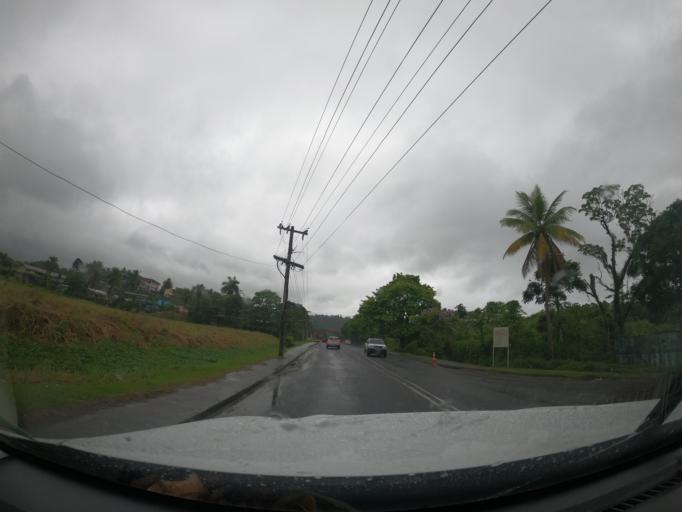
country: FJ
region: Central
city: Suva
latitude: -18.1135
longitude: 178.4274
